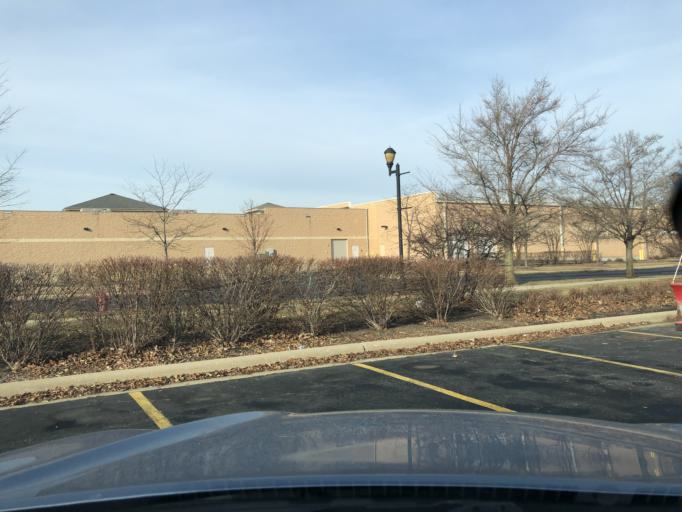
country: US
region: Illinois
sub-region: McHenry County
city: Lake in the Hills
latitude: 42.1517
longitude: -88.3328
